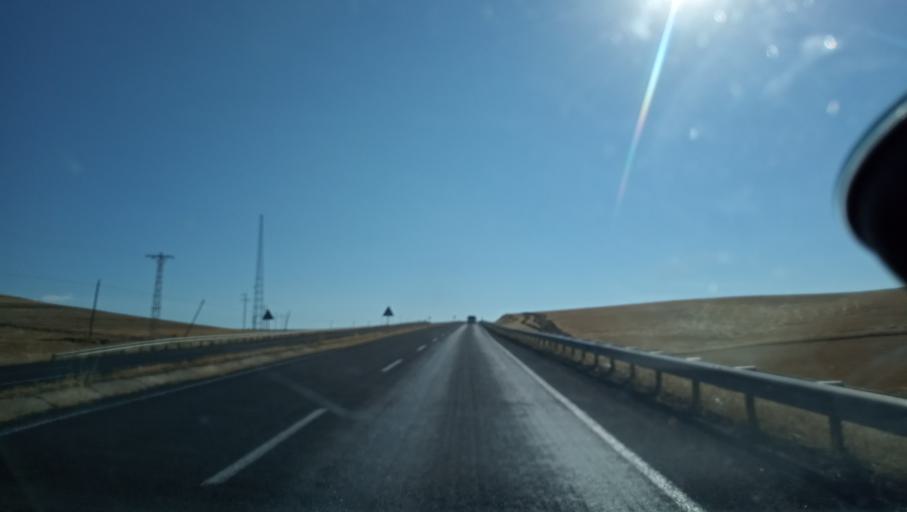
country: TR
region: Diyarbakir
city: Sur
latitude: 37.9926
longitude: 40.3968
